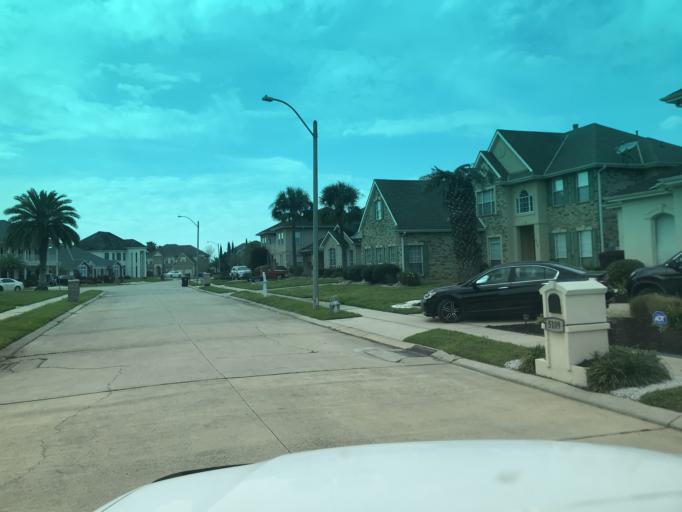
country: US
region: Louisiana
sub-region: Saint Bernard Parish
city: Chalmette
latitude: 30.0349
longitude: -89.9480
